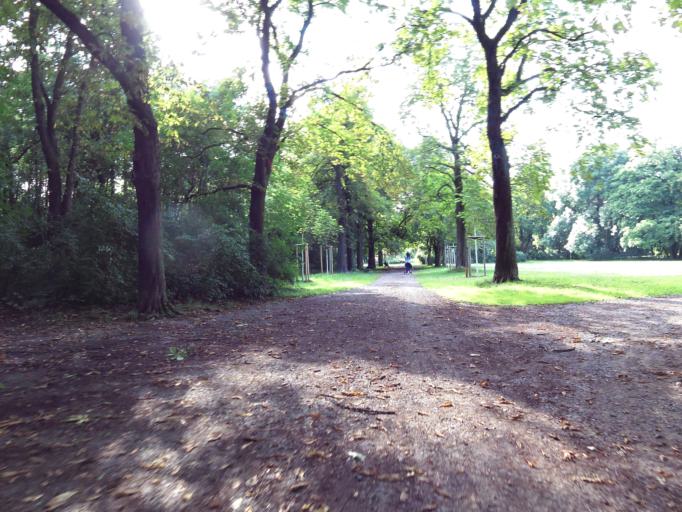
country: DE
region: Saxony
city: Leipzig
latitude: 51.3352
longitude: 12.4321
